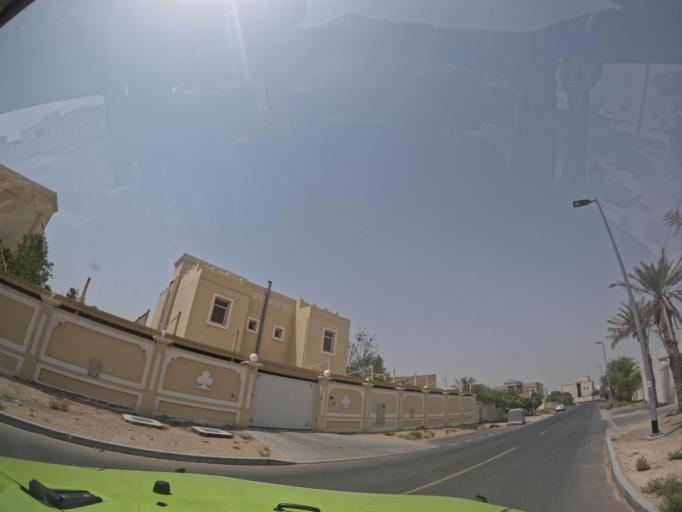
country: AE
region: Dubai
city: Dubai
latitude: 25.1332
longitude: 55.3610
